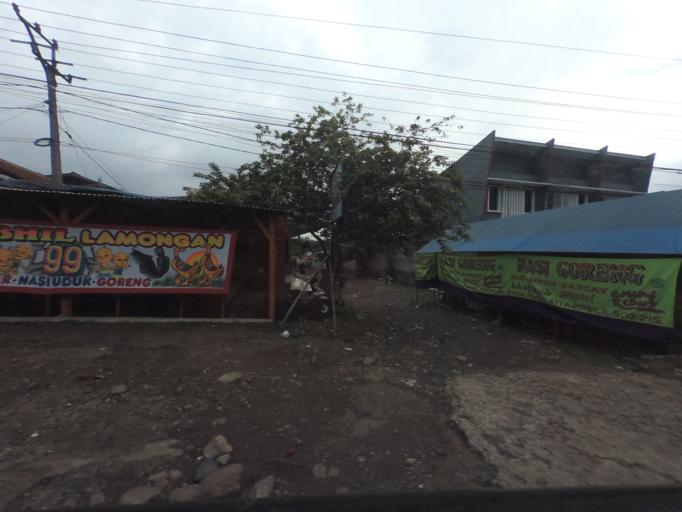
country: ID
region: West Java
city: Cicurug
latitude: -6.8336
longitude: 106.7613
